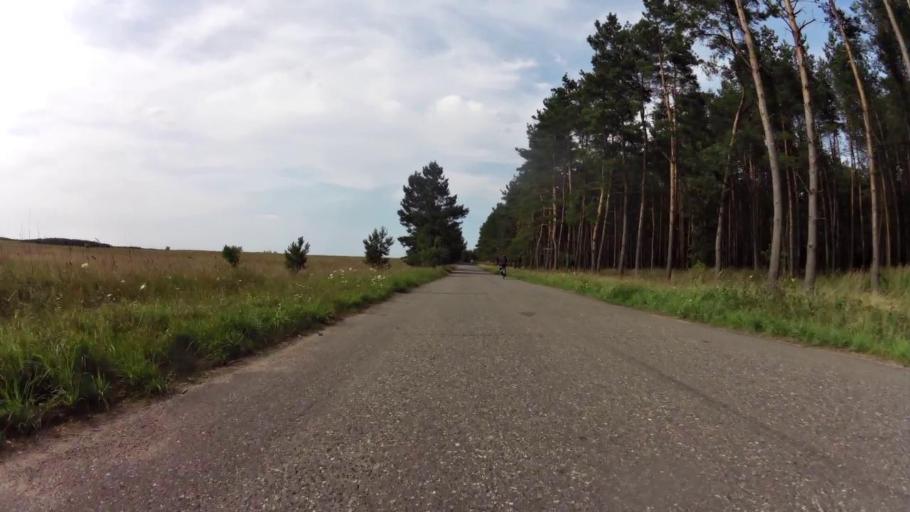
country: PL
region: West Pomeranian Voivodeship
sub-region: Powiat stargardzki
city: Insko
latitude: 53.3924
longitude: 15.5951
